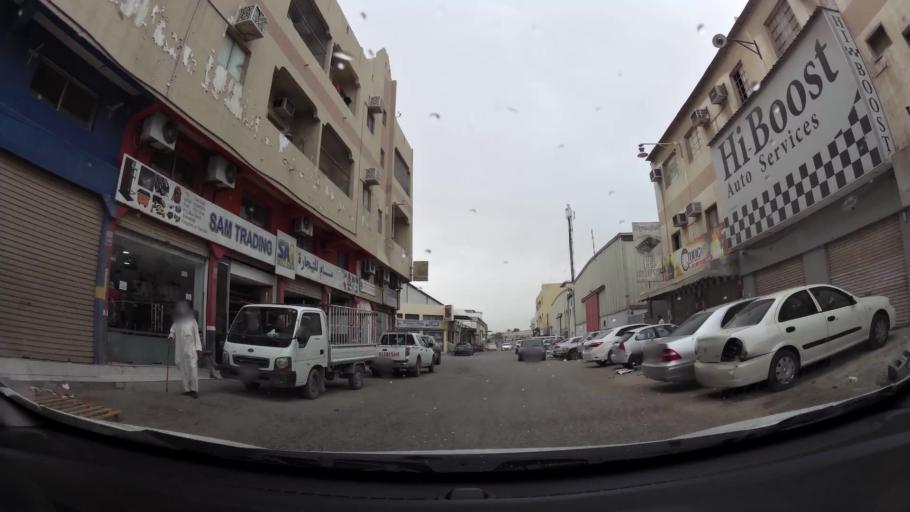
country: BH
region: Northern
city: Madinat `Isa
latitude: 26.1822
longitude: 50.5309
